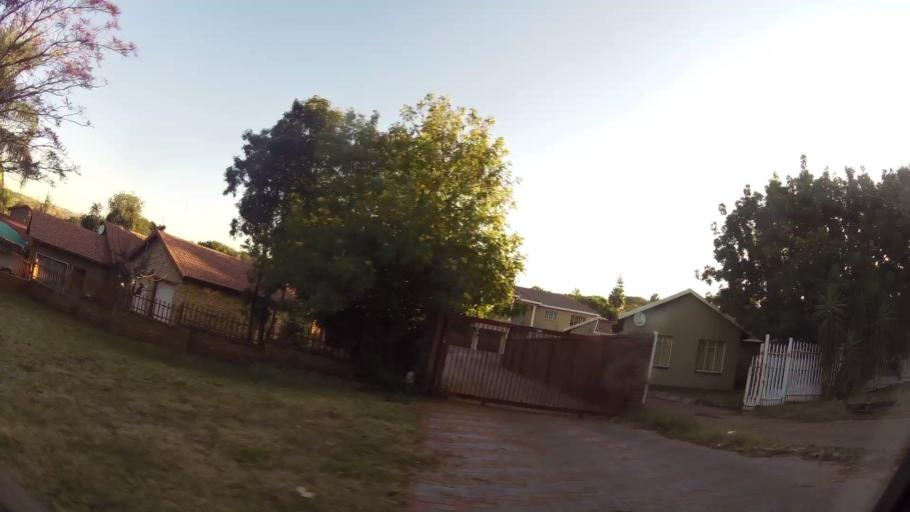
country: ZA
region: North-West
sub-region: Bojanala Platinum District Municipality
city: Rustenburg
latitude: -25.7135
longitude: 27.2371
